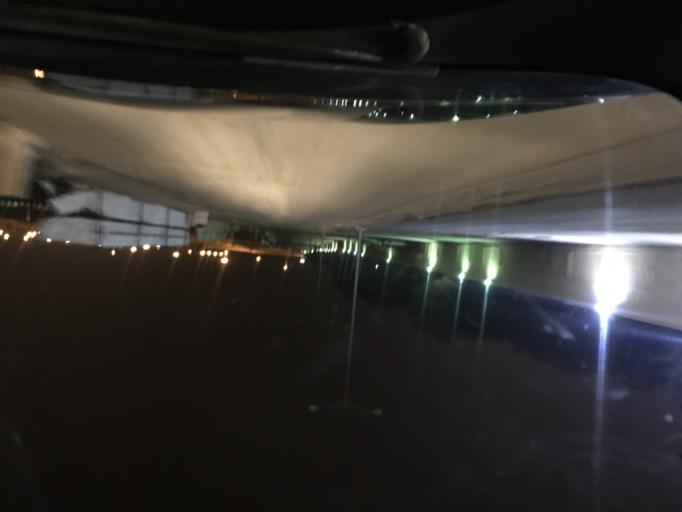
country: SA
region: Ar Riyad
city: Riyadh
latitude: 24.8115
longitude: 46.7177
